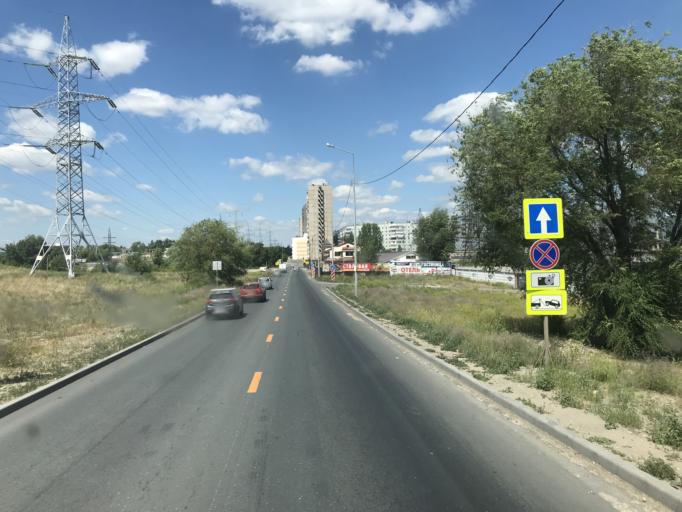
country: RU
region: Samara
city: Zhigulevsk
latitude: 53.4684
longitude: 49.5129
